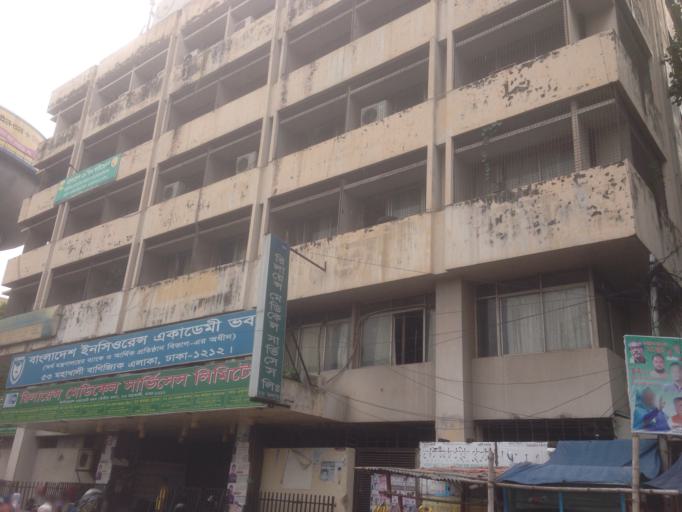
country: BD
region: Dhaka
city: Paltan
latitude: 23.7806
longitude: 90.4083
